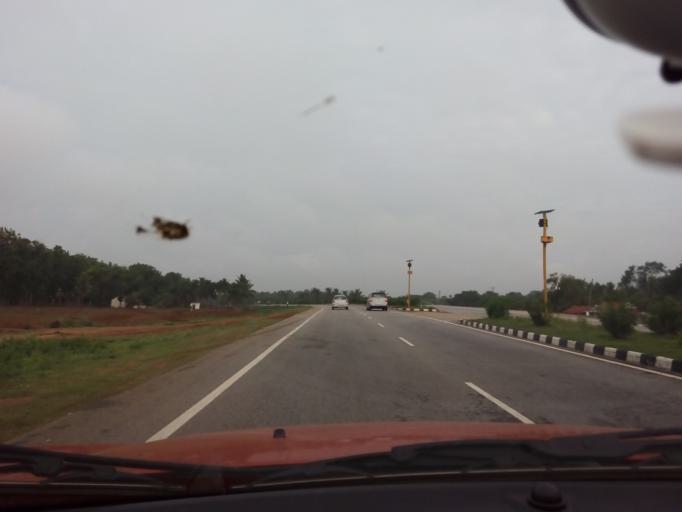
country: IN
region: Karnataka
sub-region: Tumkur
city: Kunigal
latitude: 13.0209
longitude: 77.0566
